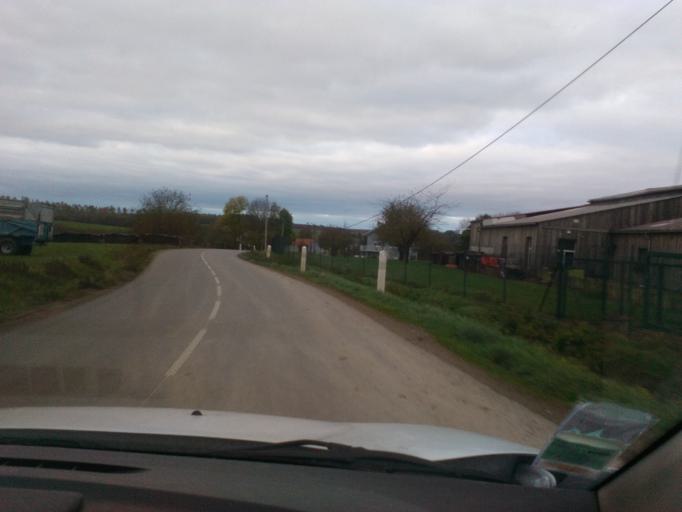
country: FR
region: Lorraine
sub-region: Departement des Vosges
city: Darnieulles
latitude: 48.2391
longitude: 6.3333
